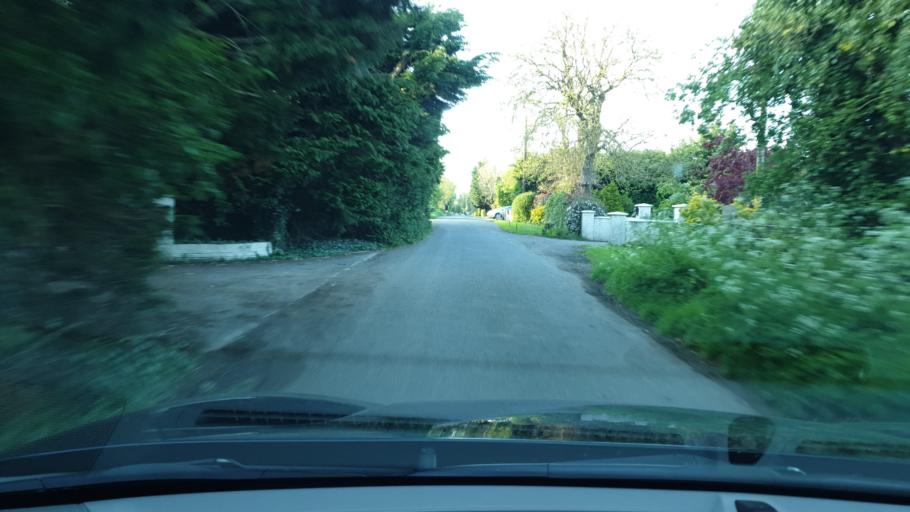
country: IE
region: Leinster
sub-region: An Mhi
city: Ashbourne
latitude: 53.4835
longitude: -6.4029
